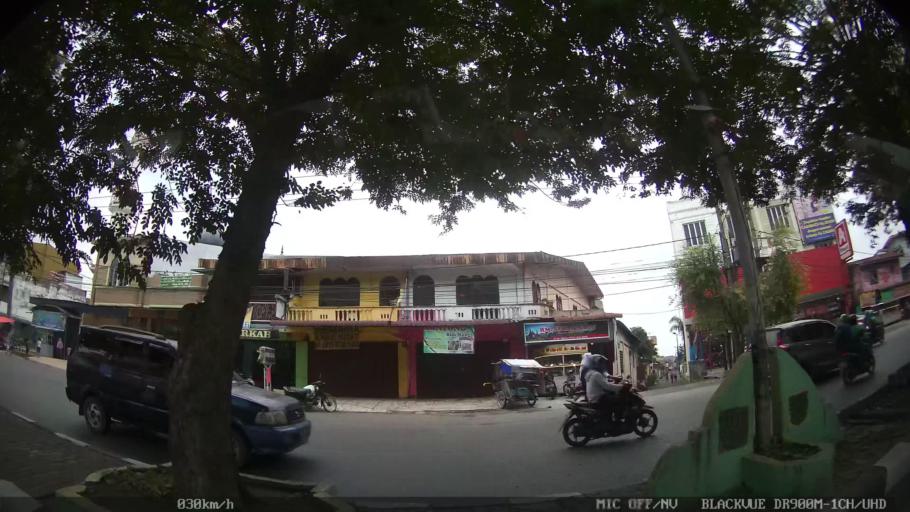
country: ID
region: North Sumatra
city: Deli Tua
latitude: 3.5506
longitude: 98.6984
